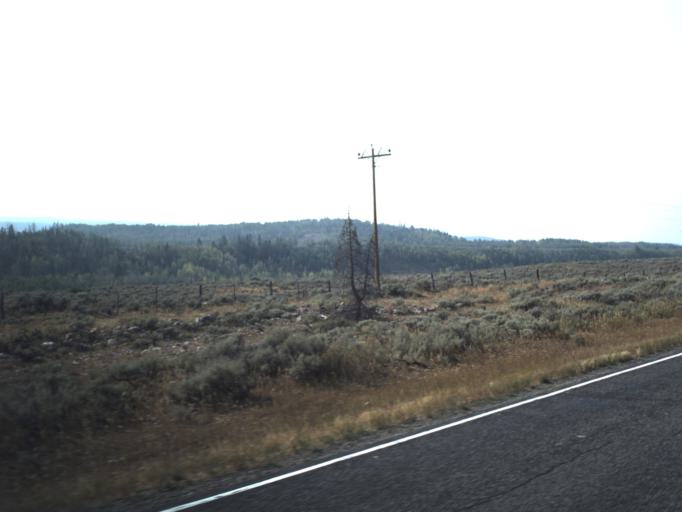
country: US
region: Wyoming
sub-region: Uinta County
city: Evanston
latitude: 40.9400
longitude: -110.8369
